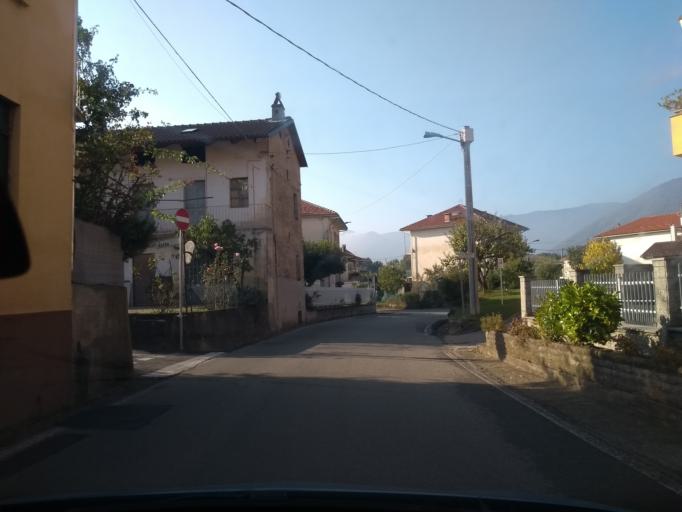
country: IT
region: Piedmont
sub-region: Provincia di Torino
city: Monasterolo
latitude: 45.2339
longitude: 7.5080
